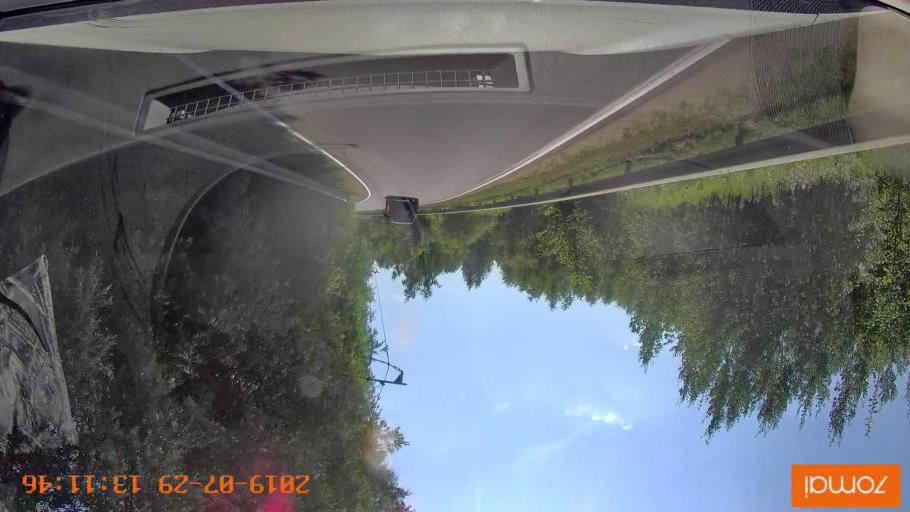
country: RU
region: Kaliningrad
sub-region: Gorod Kaliningrad
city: Kaliningrad
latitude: 54.7189
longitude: 20.3840
